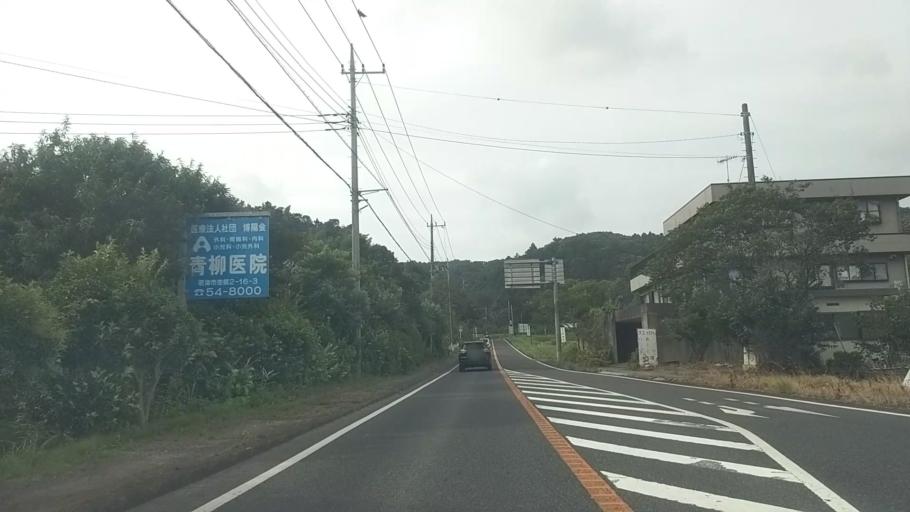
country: JP
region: Chiba
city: Kimitsu
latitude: 35.3114
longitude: 139.9621
